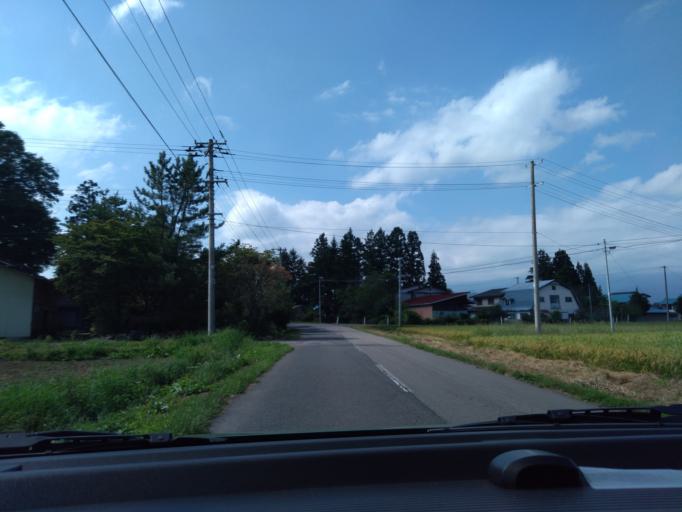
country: JP
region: Iwate
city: Shizukuishi
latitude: 39.6851
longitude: 140.9528
